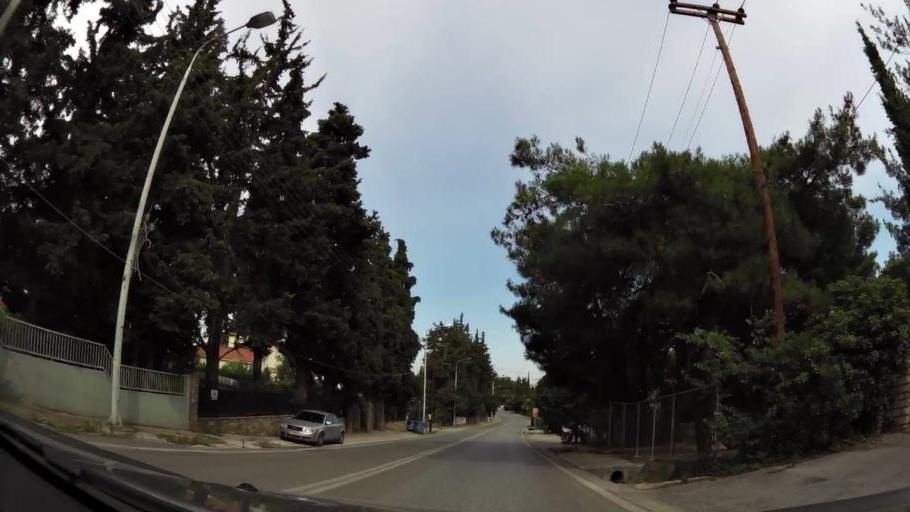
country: GR
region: Central Macedonia
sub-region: Nomos Thessalonikis
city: Panorama
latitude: 40.5928
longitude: 23.0130
